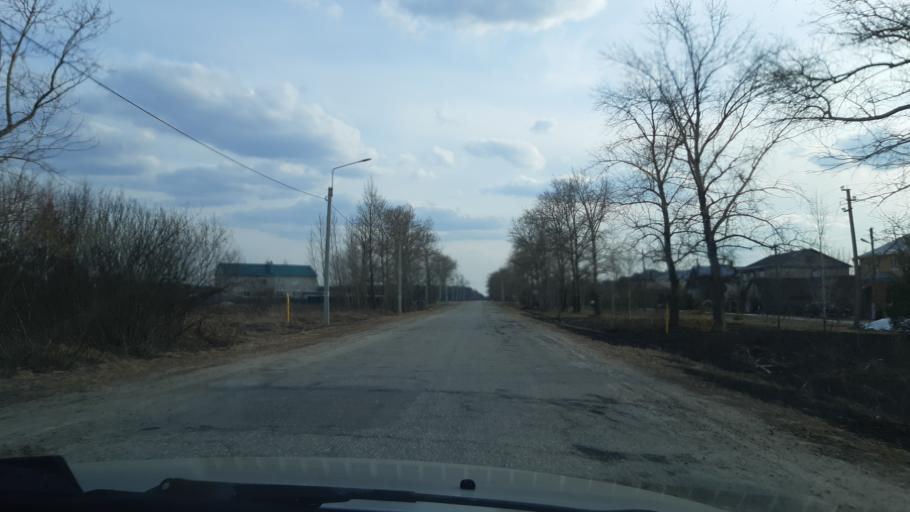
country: RU
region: Vladimir
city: Nikologory
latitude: 56.1291
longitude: 41.9896
